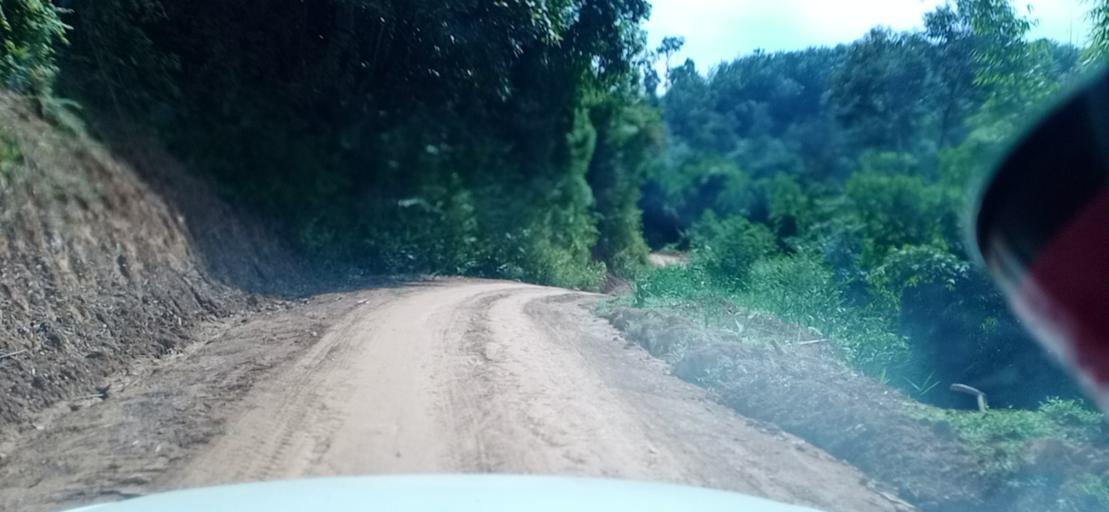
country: TH
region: Changwat Bueng Kan
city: Pak Khat
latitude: 18.6376
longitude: 103.2549
